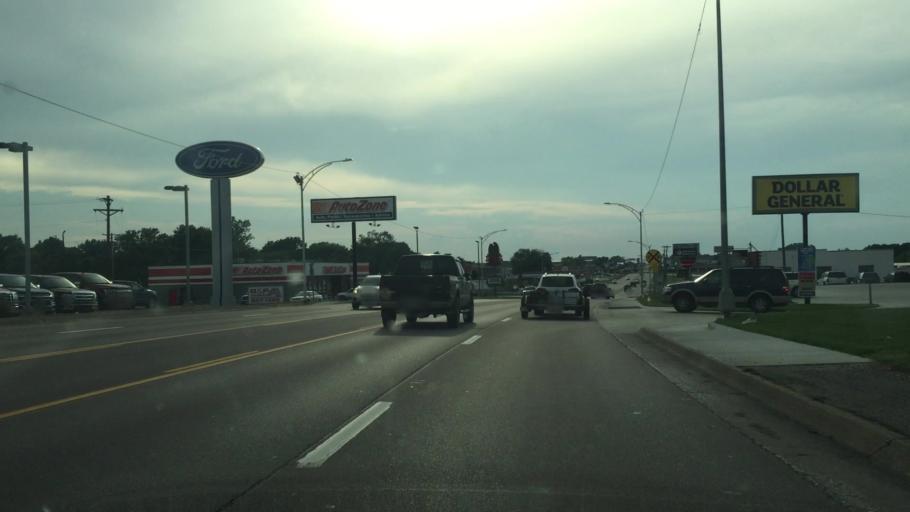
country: US
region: Missouri
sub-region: Pettis County
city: Sedalia
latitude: 38.7056
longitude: -93.2567
